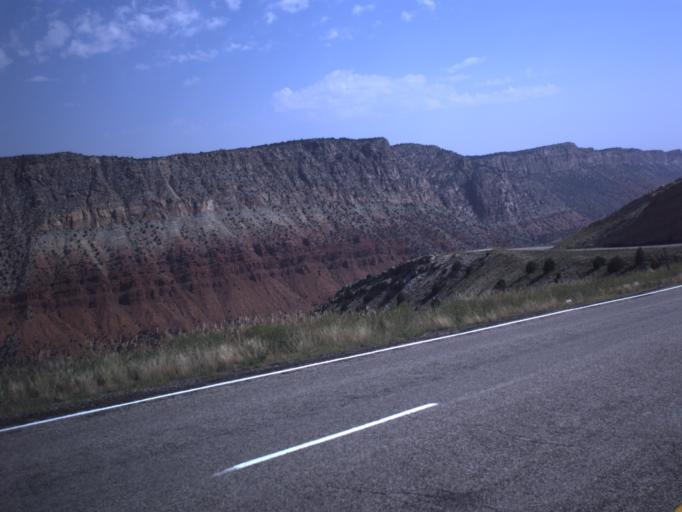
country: US
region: Utah
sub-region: Daggett County
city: Manila
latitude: 40.9097
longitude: -109.6902
